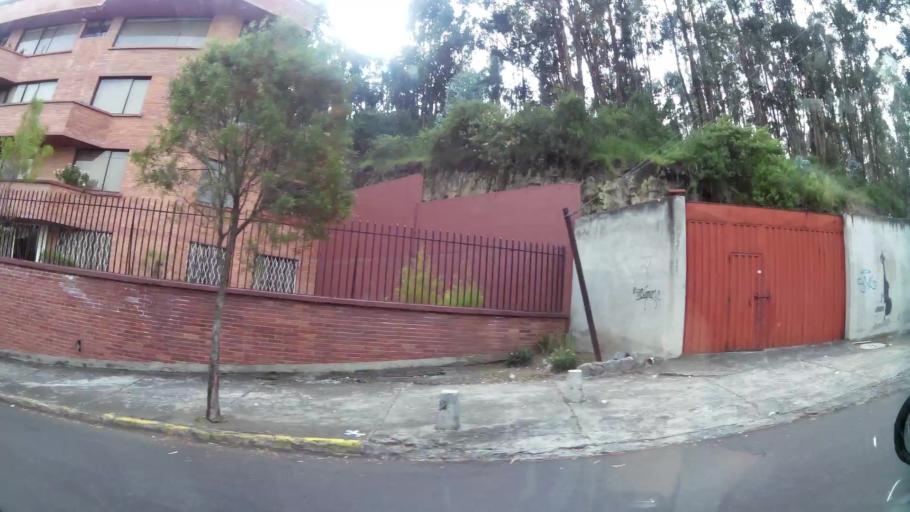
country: EC
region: Pichincha
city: Quito
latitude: -0.1737
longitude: -78.4705
